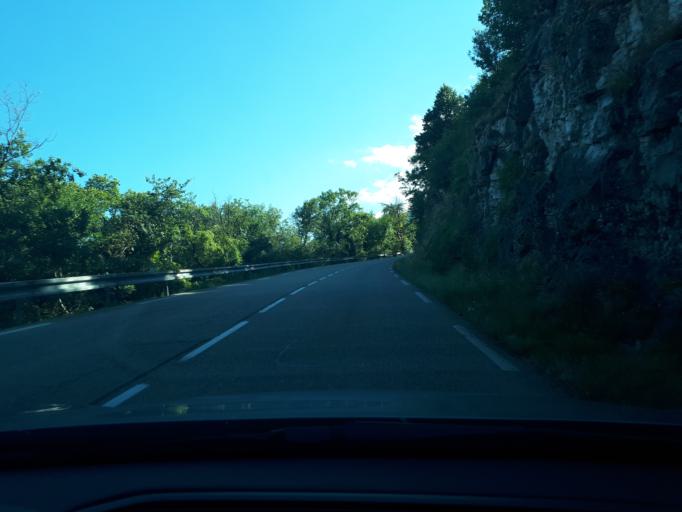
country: FR
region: Rhone-Alpes
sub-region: Departement de l'Isere
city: Seyssinet-Pariset
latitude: 45.1754
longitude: 5.6780
